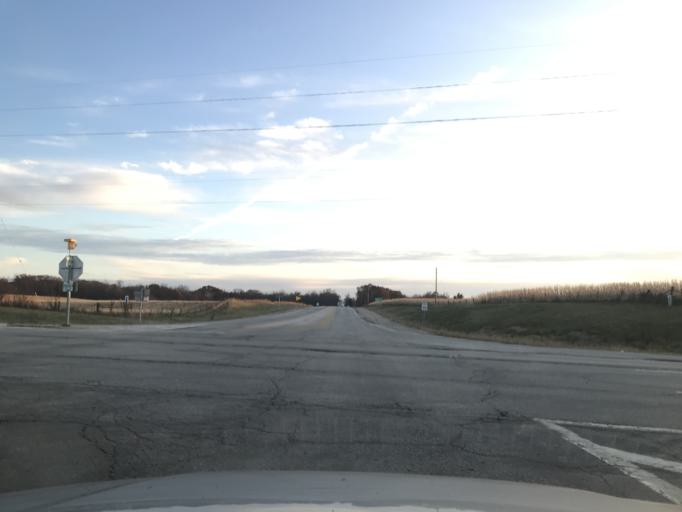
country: US
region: Illinois
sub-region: Henderson County
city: Oquawka
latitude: 40.9238
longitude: -90.8642
